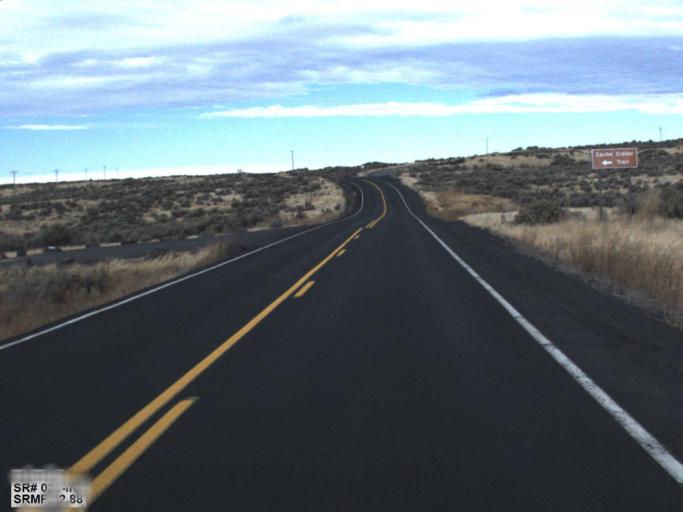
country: US
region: Washington
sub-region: Adams County
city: Ritzville
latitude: 47.4230
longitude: -118.6978
